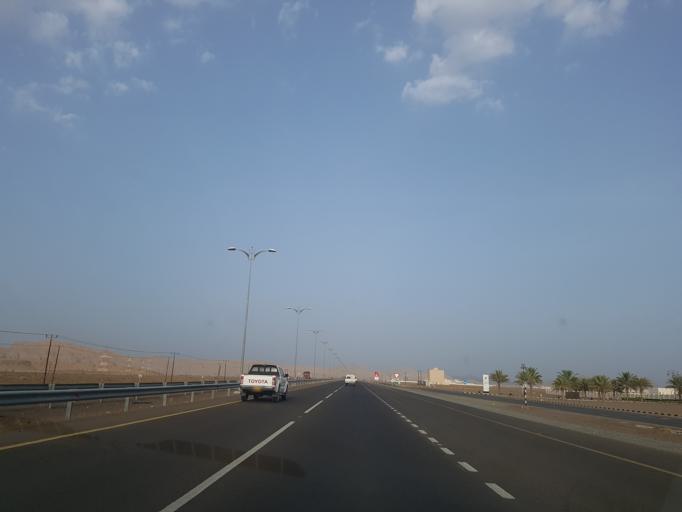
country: OM
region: Al Buraimi
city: Al Buraymi
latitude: 24.2378
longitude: 55.8950
